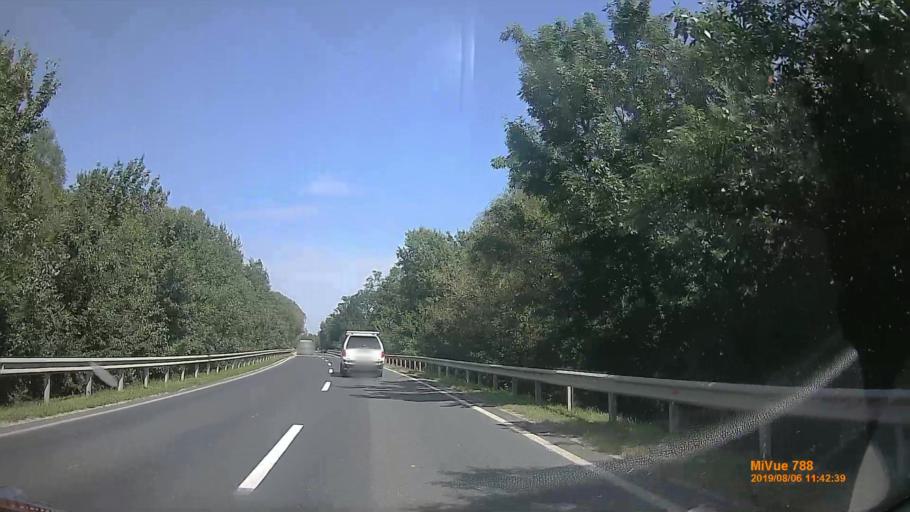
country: HU
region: Vas
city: Kormend
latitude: 46.9998
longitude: 16.5451
